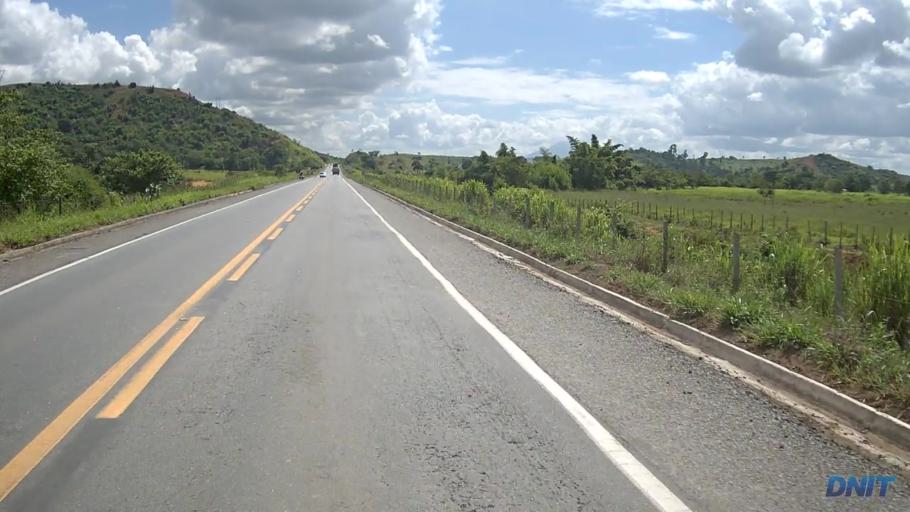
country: BR
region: Minas Gerais
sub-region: Governador Valadares
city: Governador Valadares
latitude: -19.0017
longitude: -42.1265
